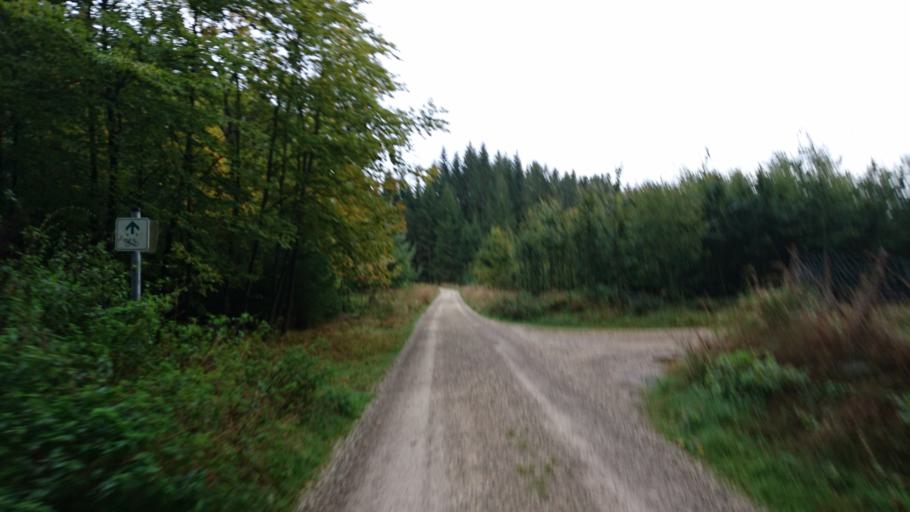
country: DE
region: Bavaria
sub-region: Swabia
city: Welden
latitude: 48.4373
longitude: 10.6434
